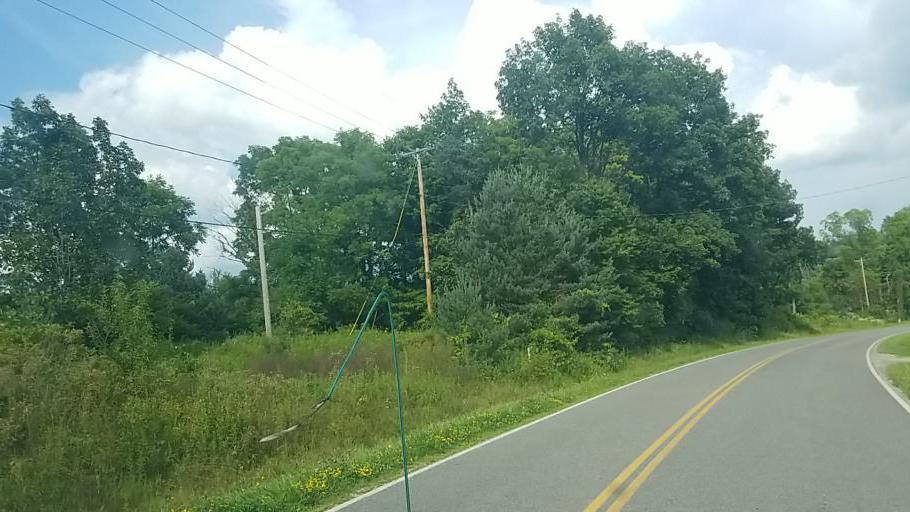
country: US
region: Ohio
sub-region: Medina County
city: Westfield Center
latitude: 41.0121
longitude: -81.9360
